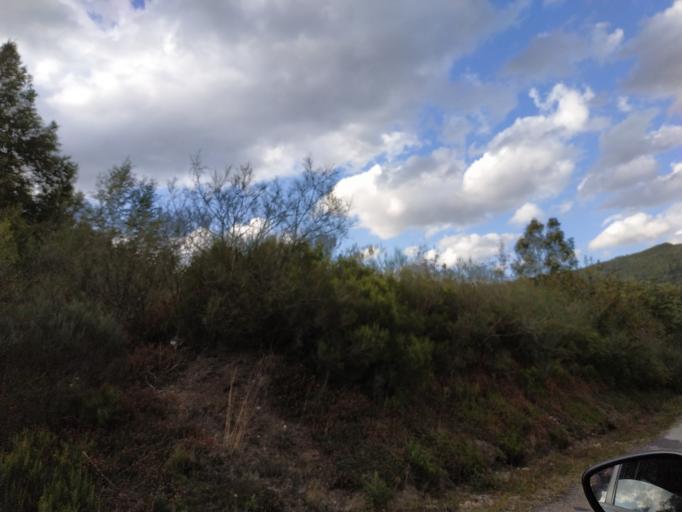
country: ES
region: Castille and Leon
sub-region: Provincia de Leon
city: Candin
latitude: 42.8624
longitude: -6.8642
